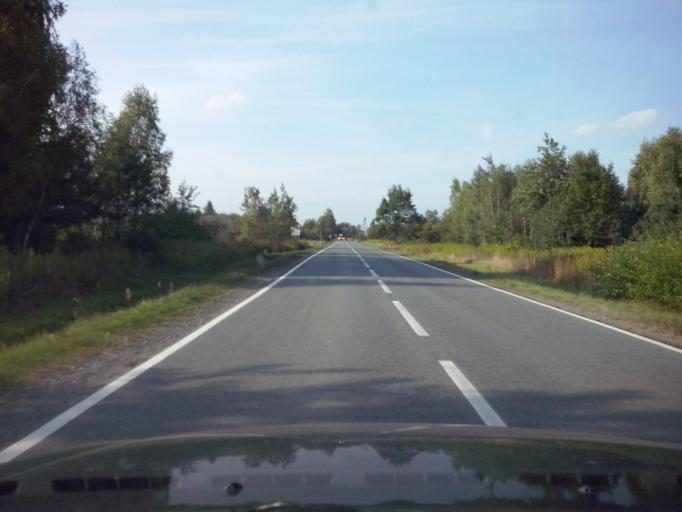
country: PL
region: Subcarpathian Voivodeship
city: Nowa Sarzyna
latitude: 50.3512
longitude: 22.3228
